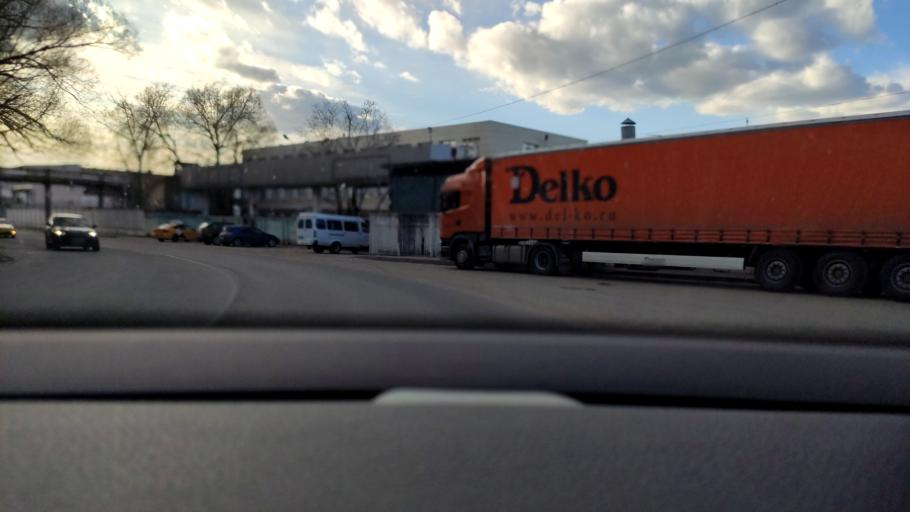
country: RU
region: Moskovskaya
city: Reutov
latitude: 55.7721
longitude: 37.8776
